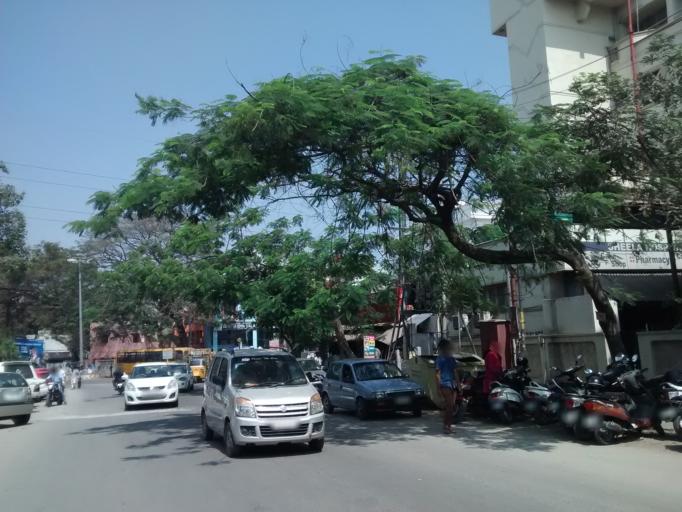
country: IN
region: Tamil Nadu
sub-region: Coimbatore
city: Coimbatore
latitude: 11.0183
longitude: 76.9602
